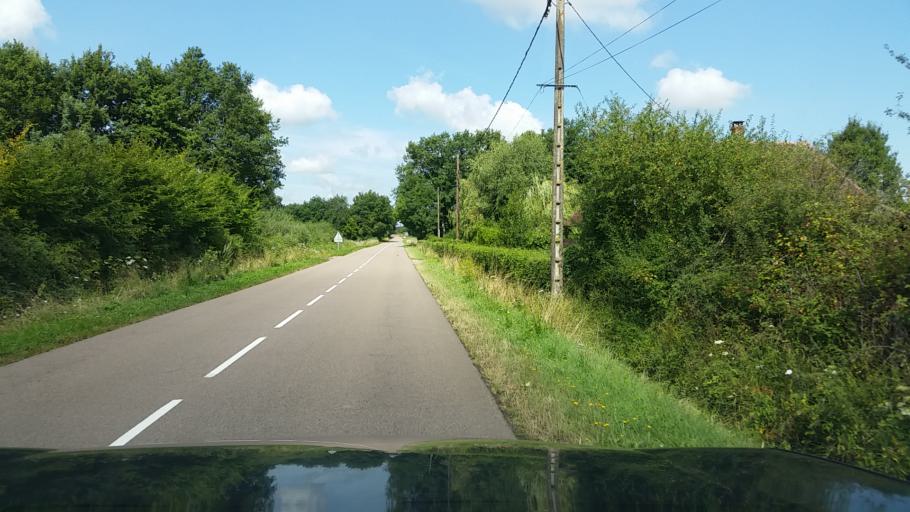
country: FR
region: Bourgogne
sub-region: Departement de Saone-et-Loire
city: Saint-Germain-du-Bois
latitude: 46.7341
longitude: 5.2667
